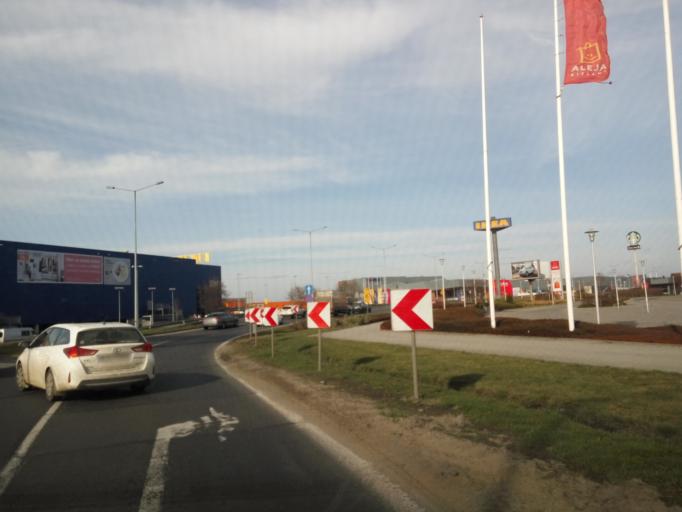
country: PL
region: Lower Silesian Voivodeship
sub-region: Powiat wroclawski
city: Bielany Wroclawskie
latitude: 51.0459
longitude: 16.9556
